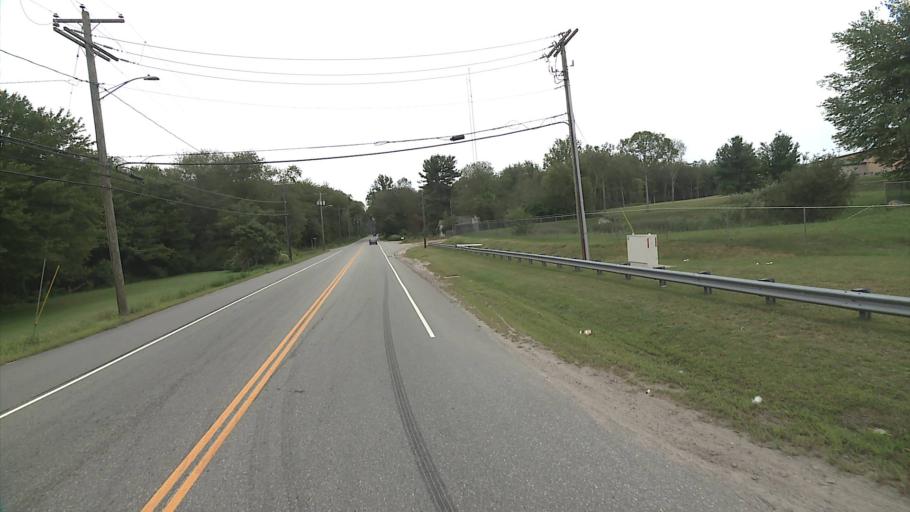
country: US
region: Connecticut
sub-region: New London County
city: Montville Center
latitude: 41.4244
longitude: -72.2066
